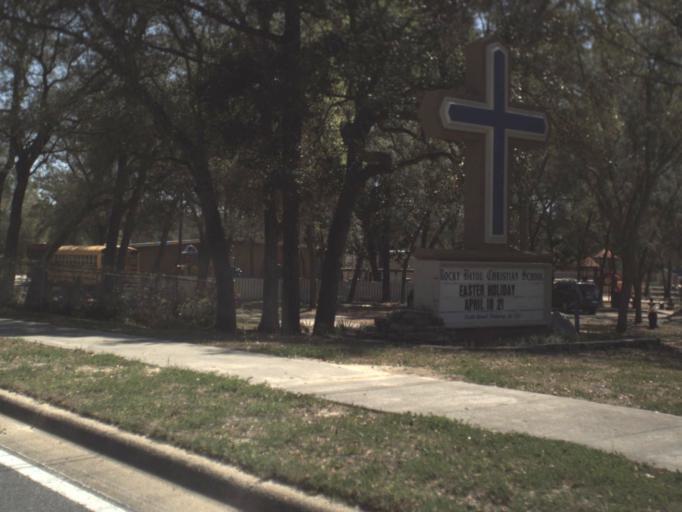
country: US
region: Florida
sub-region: Okaloosa County
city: Niceville
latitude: 30.5288
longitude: -86.4625
